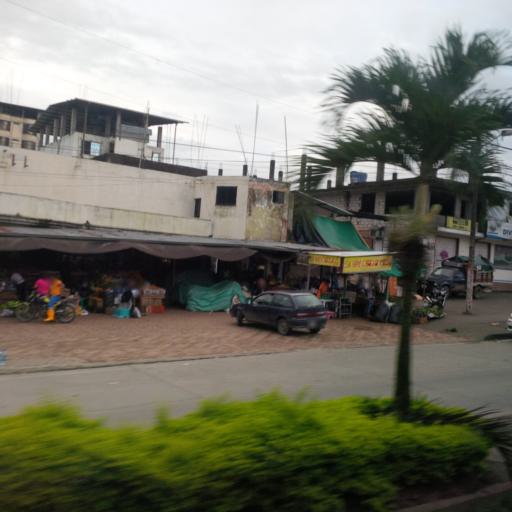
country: EC
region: Chimborazo
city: Alausi
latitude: -2.2059
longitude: -79.1333
